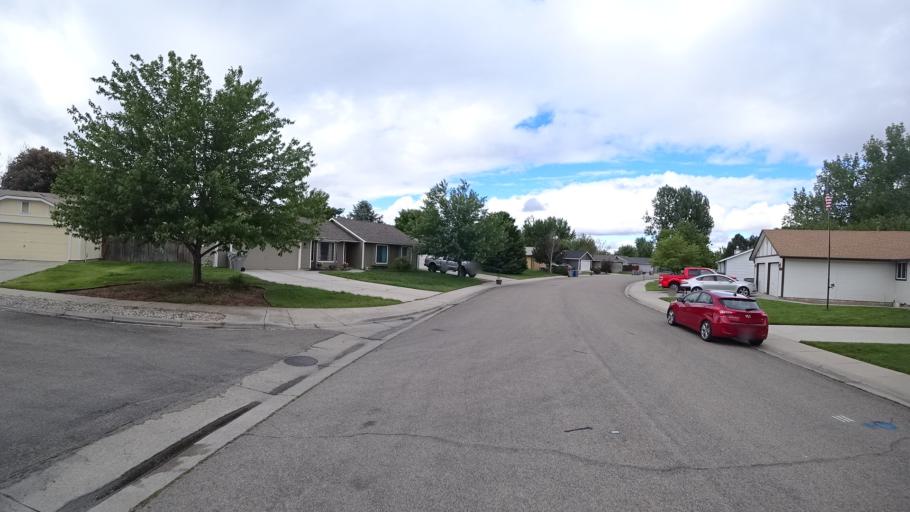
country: US
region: Idaho
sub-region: Ada County
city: Garden City
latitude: 43.6711
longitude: -116.2758
